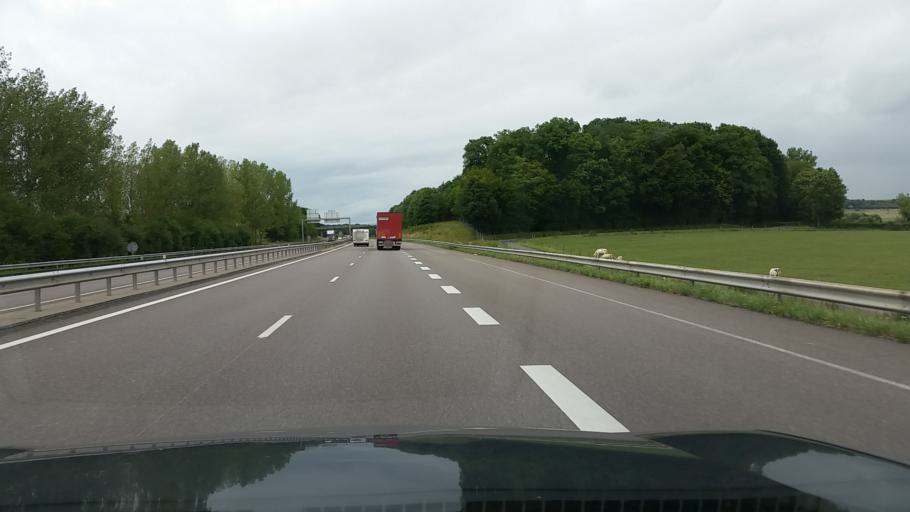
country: FR
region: Lorraine
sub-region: Departement des Vosges
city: Chatenois
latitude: 48.3016
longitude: 5.8575
